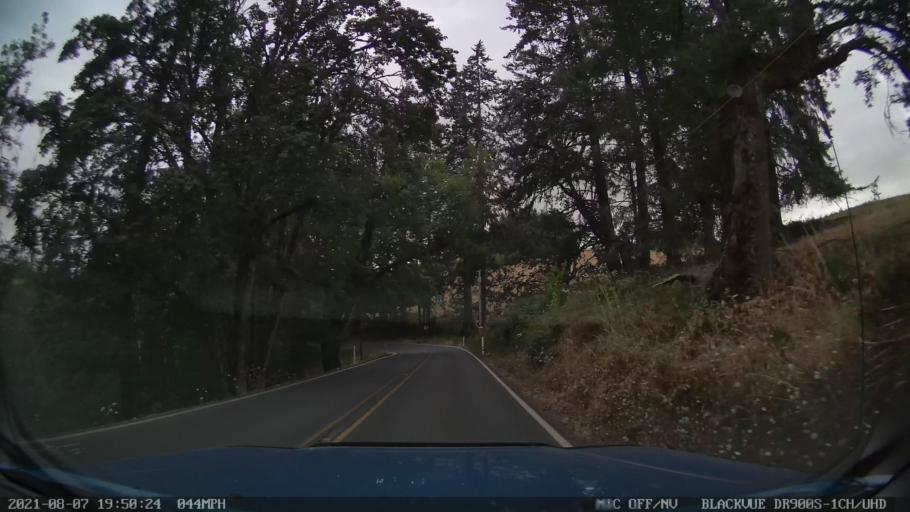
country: US
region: Oregon
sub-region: Marion County
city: Silverton
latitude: 44.9859
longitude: -122.7382
